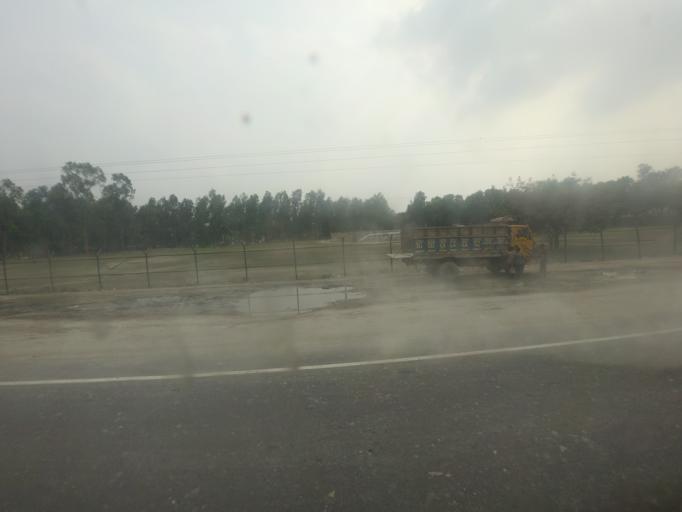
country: BD
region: Rajshahi
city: Sirajganj
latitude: 24.3891
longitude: 89.8199
